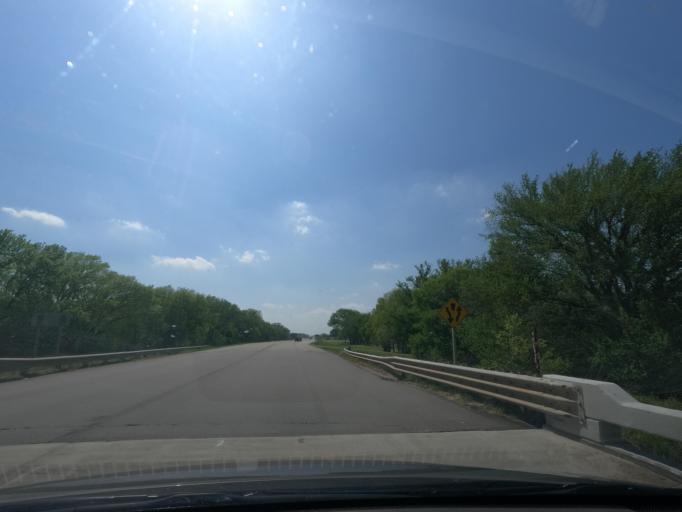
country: US
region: Kansas
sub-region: Butler County
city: Clay Center
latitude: 37.6796
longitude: -96.7790
